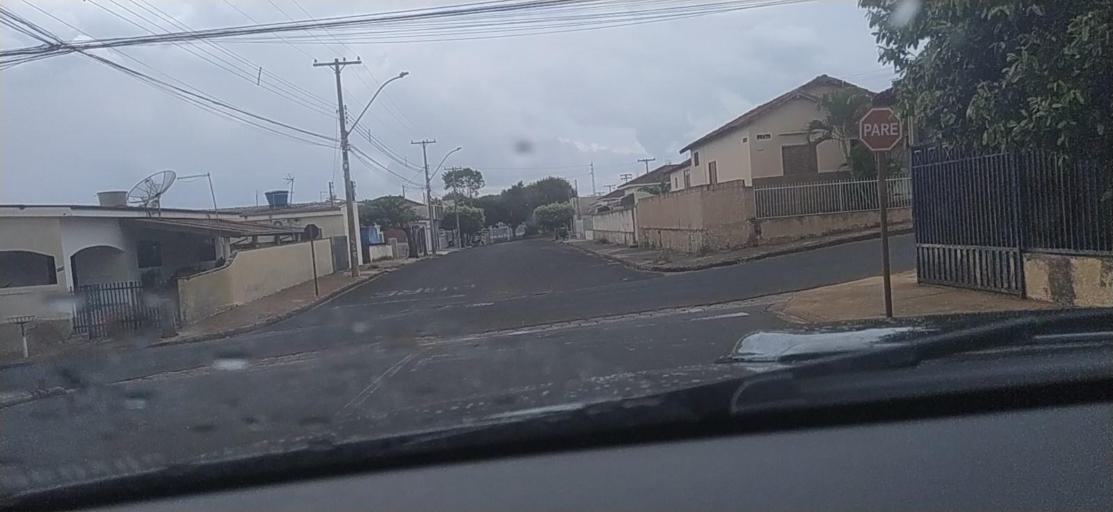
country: BR
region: Sao Paulo
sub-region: Pindorama
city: Pindorama
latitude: -21.1870
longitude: -48.9002
